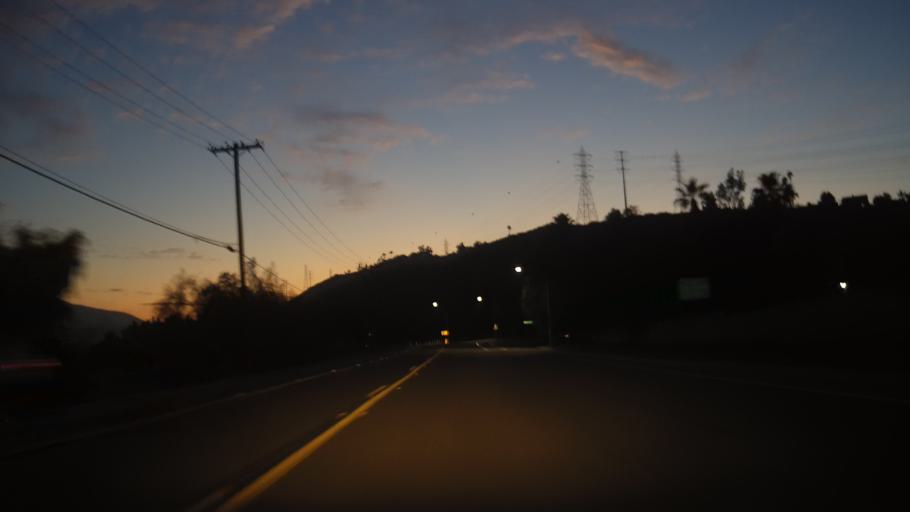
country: US
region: California
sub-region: San Diego County
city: Rancho San Diego
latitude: 32.7582
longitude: -116.9013
